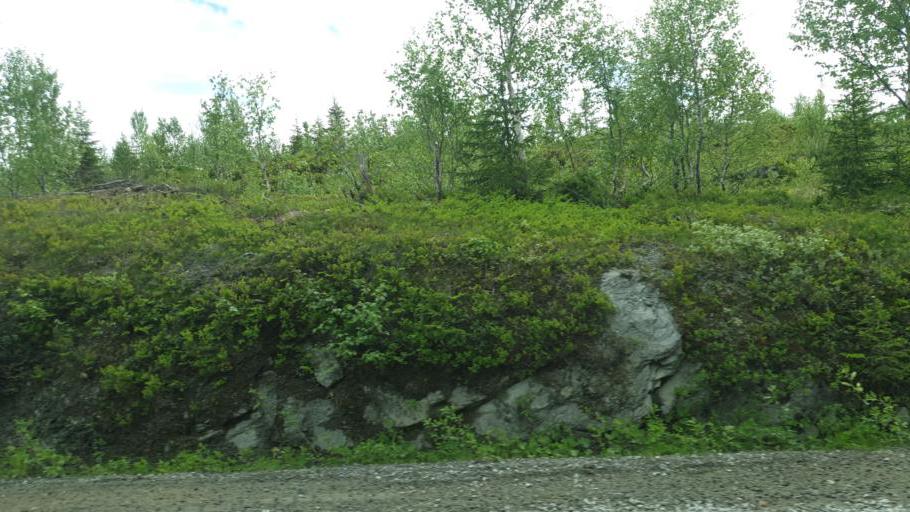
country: NO
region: Nord-Trondelag
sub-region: Leksvik
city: Leksvik
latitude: 63.6870
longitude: 10.3932
